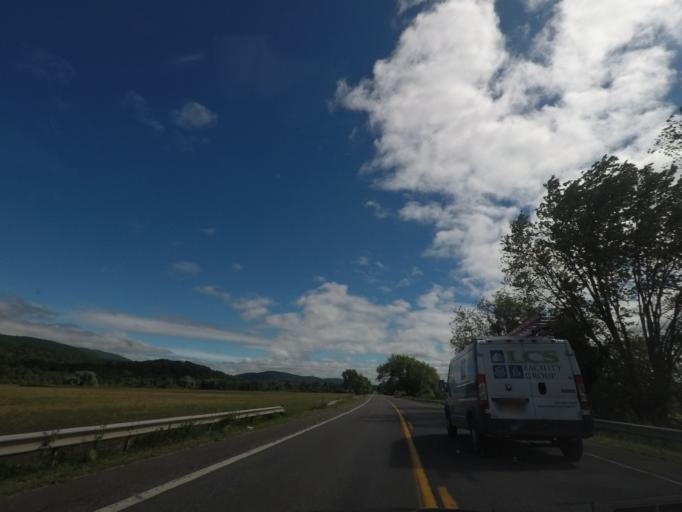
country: US
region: New York
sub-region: Dutchess County
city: Pine Plains
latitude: 42.1040
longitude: -73.5408
